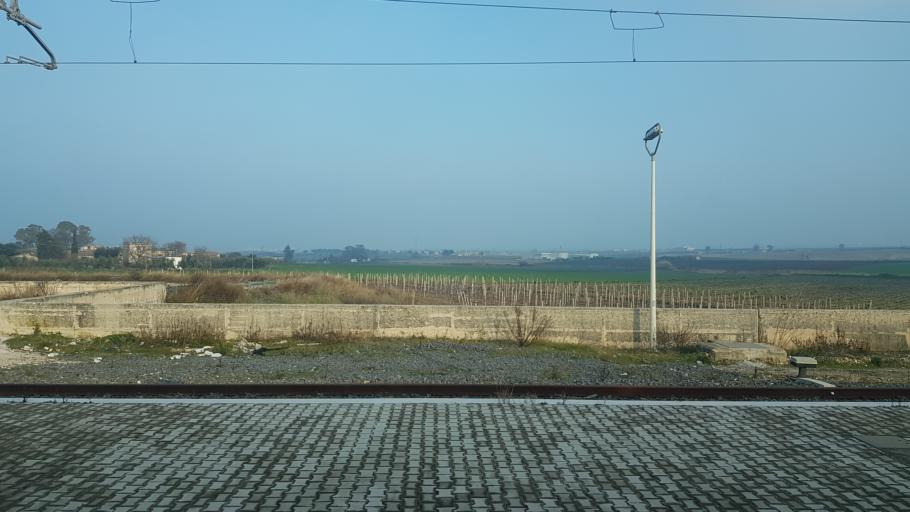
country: IT
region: Apulia
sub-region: Provincia di Foggia
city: Lesina
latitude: 41.8538
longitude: 15.2958
